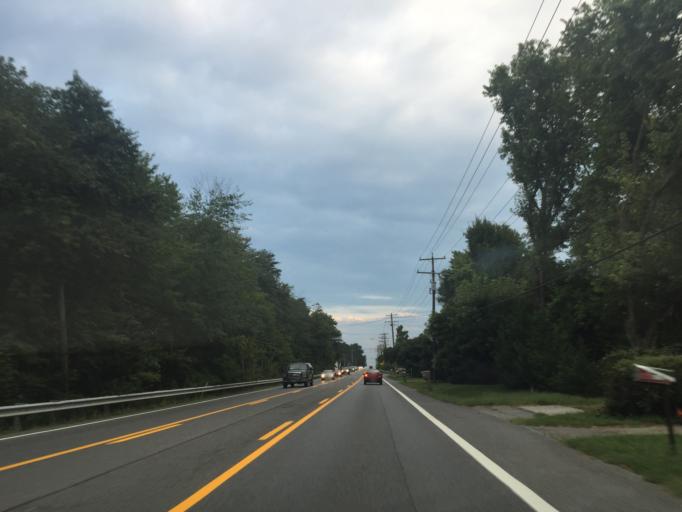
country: US
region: Maryland
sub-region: Anne Arundel County
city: Severn
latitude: 39.1122
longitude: -76.6921
